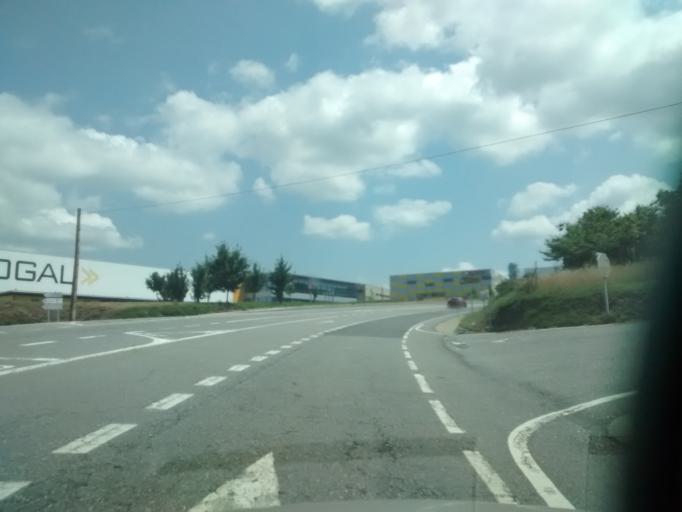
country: ES
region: Galicia
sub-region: Provincia de Pontevedra
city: Forcarei
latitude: 42.5402
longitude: -8.3142
